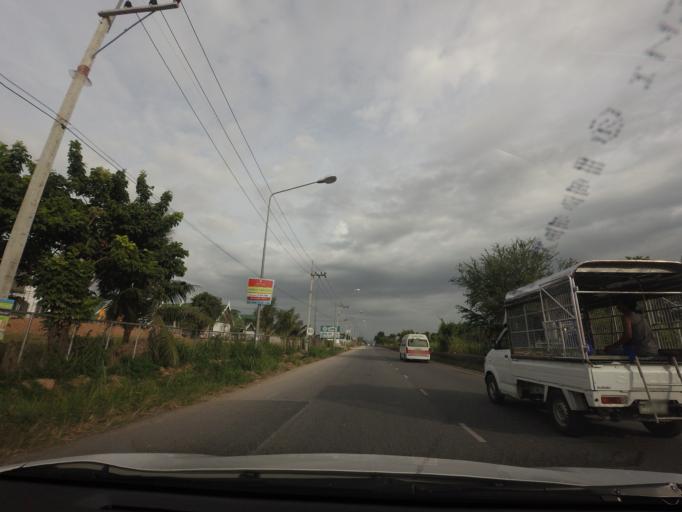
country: TH
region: Chon Buri
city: Phatthaya
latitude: 12.8771
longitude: 100.9068
